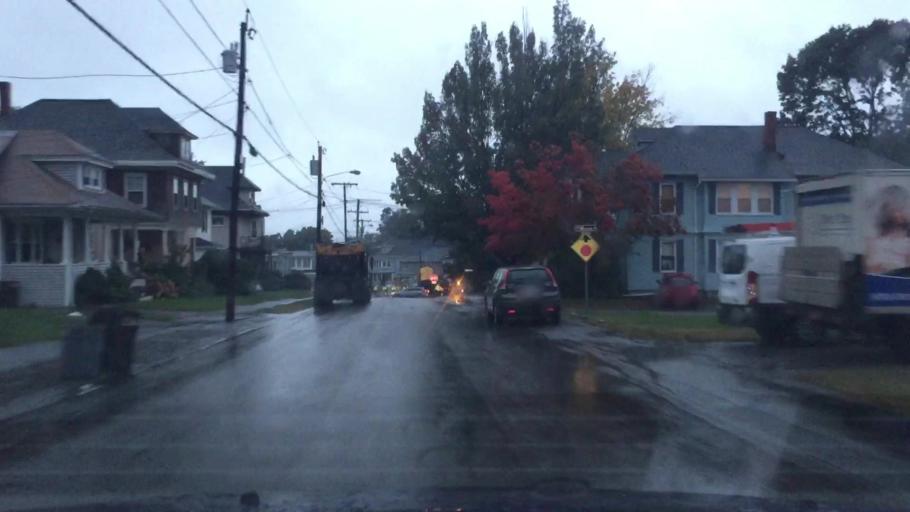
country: US
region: Massachusetts
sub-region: Essex County
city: North Andover
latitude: 42.6987
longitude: -71.1331
